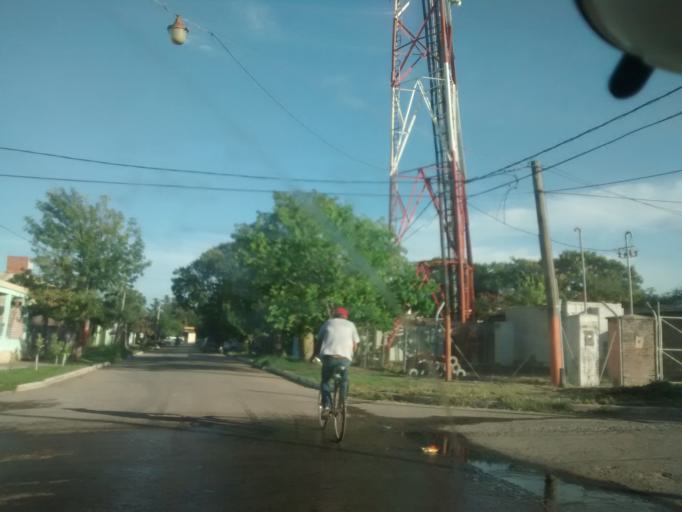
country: AR
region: Chaco
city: Resistencia
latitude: -27.4580
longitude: -59.0046
